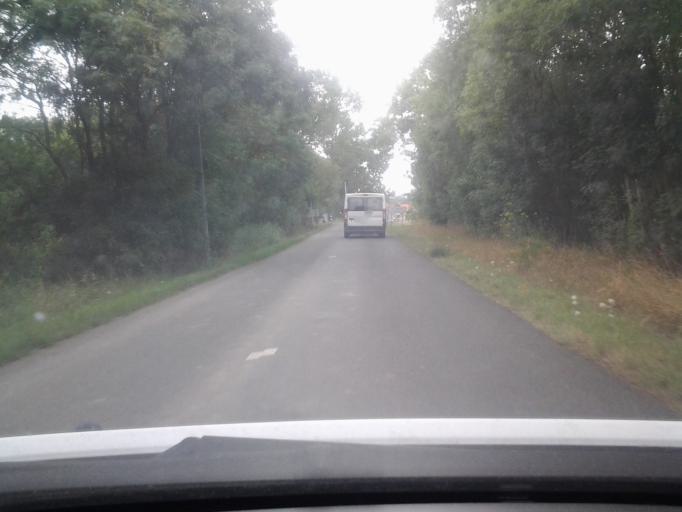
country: FR
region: Pays de la Loire
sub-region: Departement de la Vendee
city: Longeville-sur-Mer
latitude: 46.3872
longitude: -1.4616
